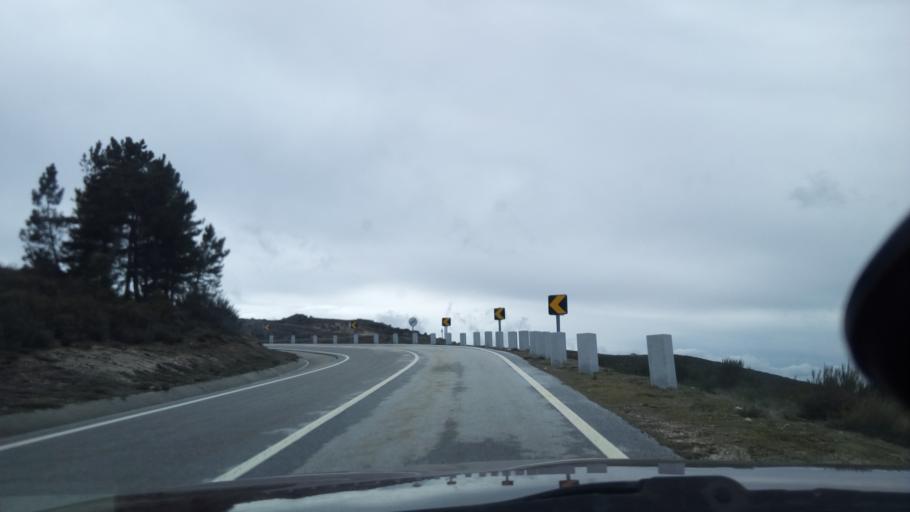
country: PT
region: Guarda
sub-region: Seia
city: Seia
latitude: 40.3498
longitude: -7.7009
